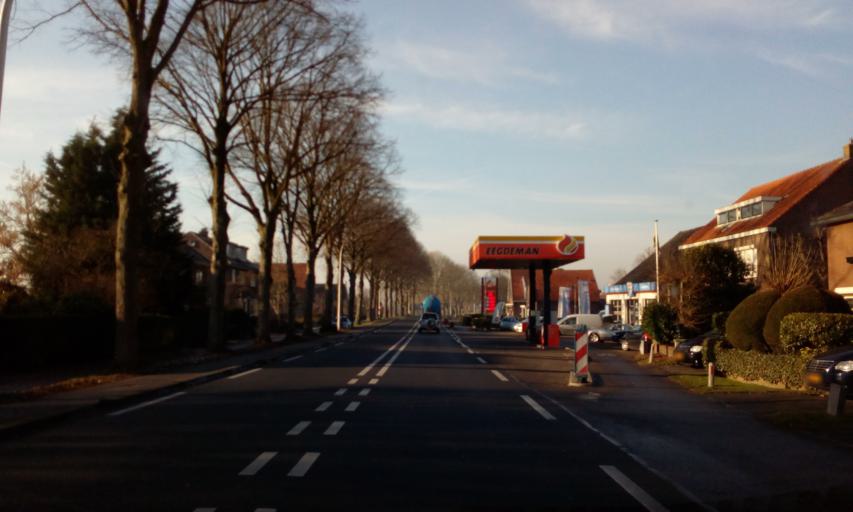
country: NL
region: South Holland
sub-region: Gemeente Vlist
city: Haastrecht
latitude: 52.0009
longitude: 4.7679
